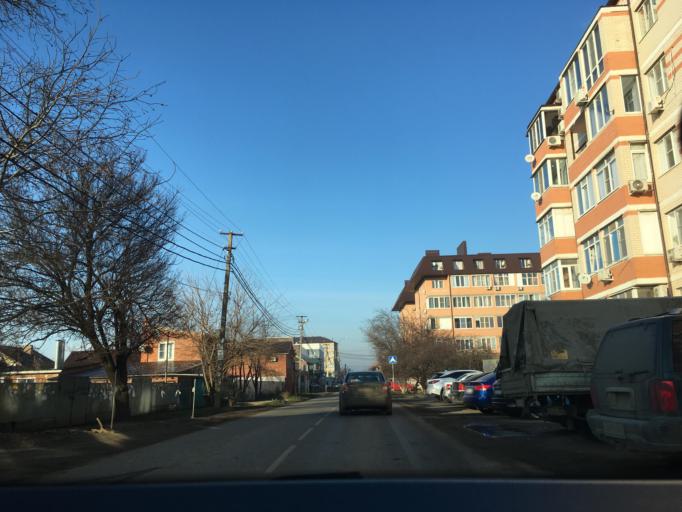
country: RU
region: Krasnodarskiy
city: Krasnodar
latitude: 45.0737
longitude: 39.0212
